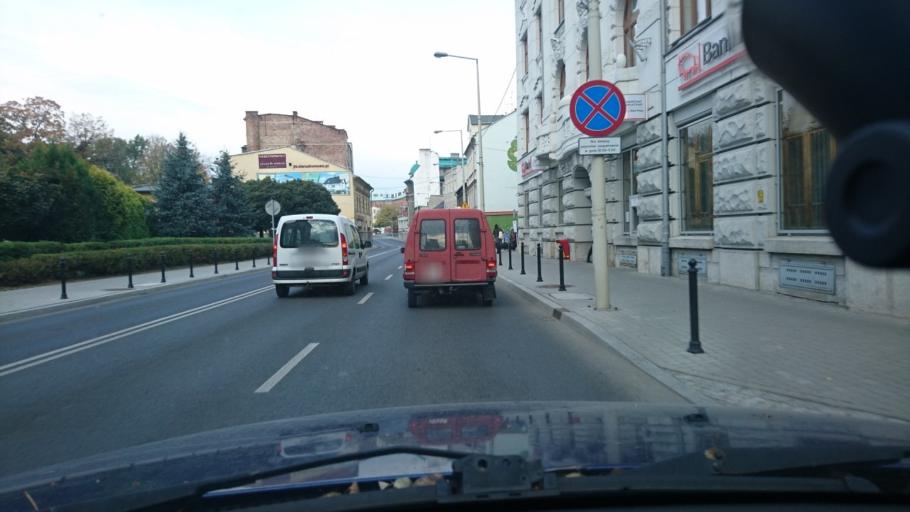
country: PL
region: Silesian Voivodeship
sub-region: Bielsko-Biala
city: Bielsko-Biala
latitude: 49.8224
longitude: 19.0511
